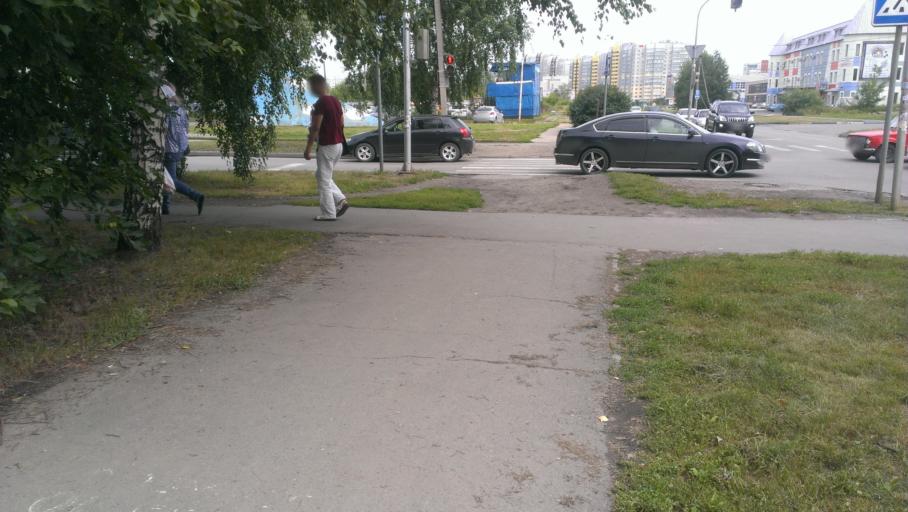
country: RU
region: Altai Krai
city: Novosilikatnyy
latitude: 53.3389
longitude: 83.6777
